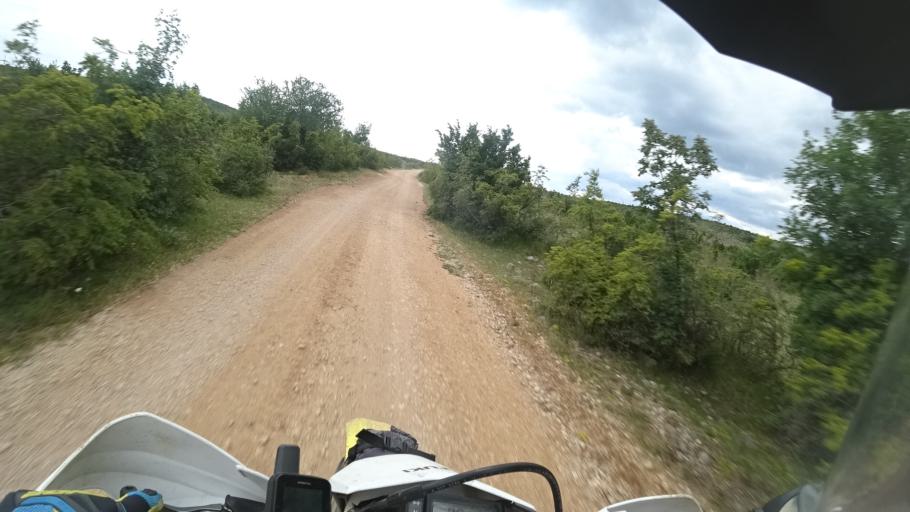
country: HR
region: Sibensko-Kniniska
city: Kistanje
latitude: 44.0949
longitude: 16.0011
